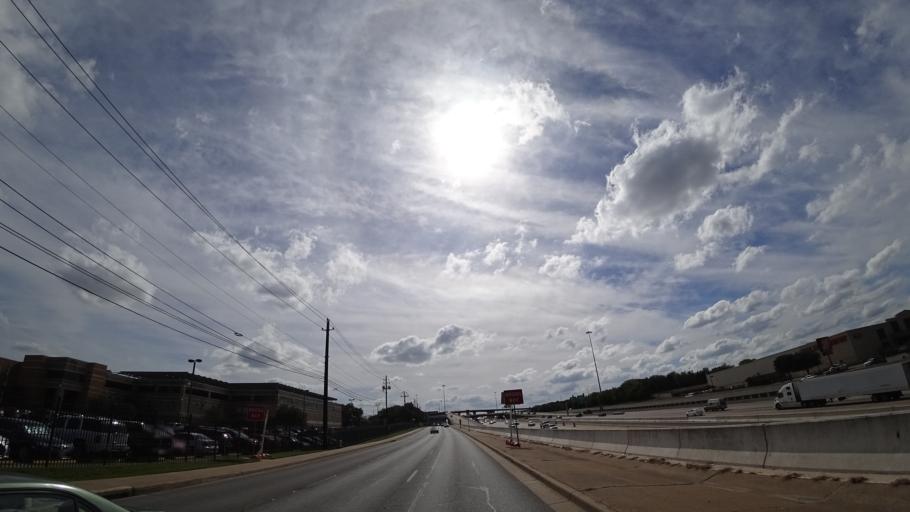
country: US
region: Texas
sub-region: Travis County
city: Austin
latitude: 30.2224
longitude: -97.7474
